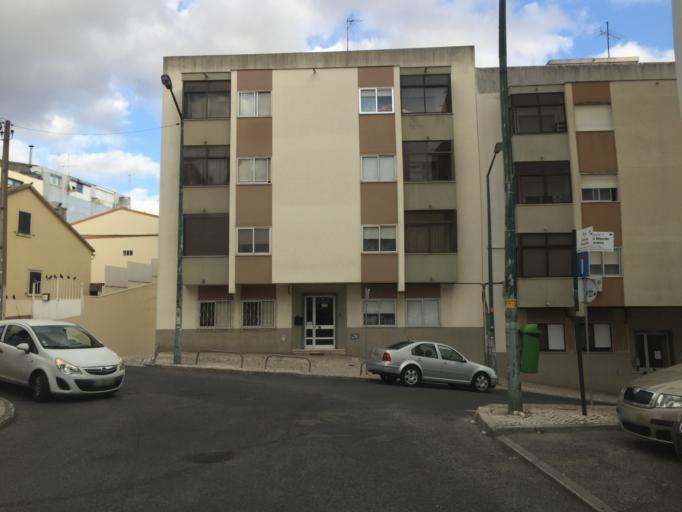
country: PT
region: Lisbon
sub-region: Odivelas
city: Ramada
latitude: 38.8009
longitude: -9.1862
